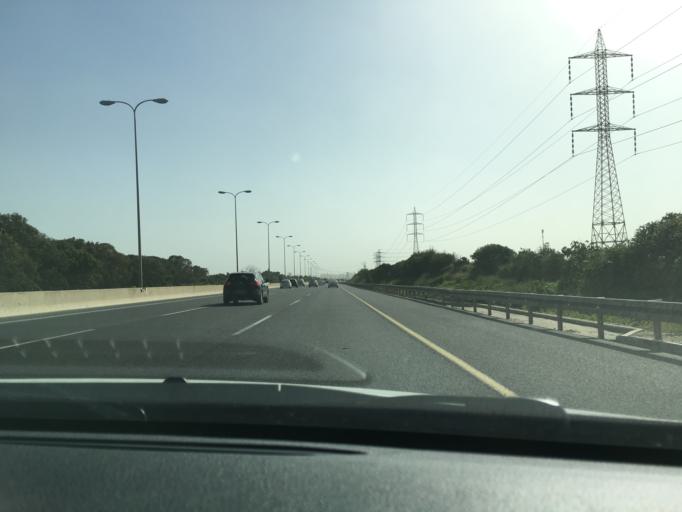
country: IL
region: Central District
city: Hod HaSharon
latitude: 32.1519
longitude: 34.8725
